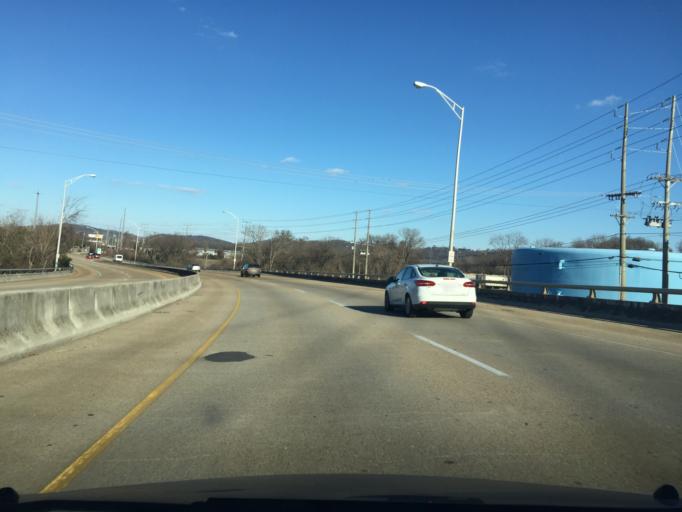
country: US
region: Tennessee
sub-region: Hamilton County
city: Chattanooga
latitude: 35.0523
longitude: -85.2888
